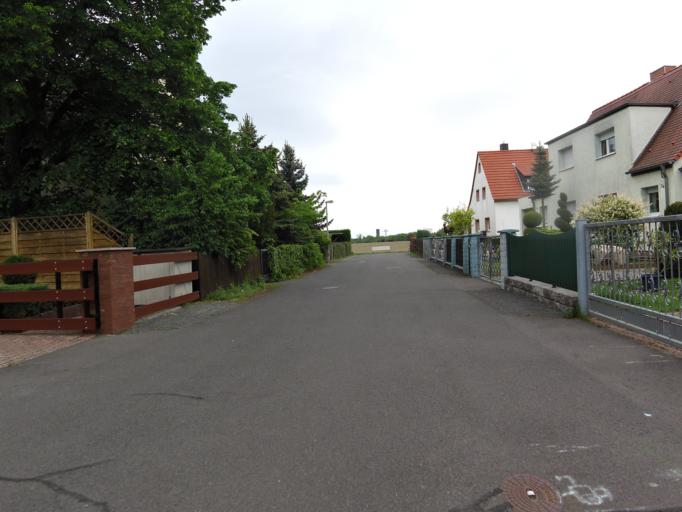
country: DE
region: Saxony
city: Markkleeberg
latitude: 51.2863
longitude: 12.3102
